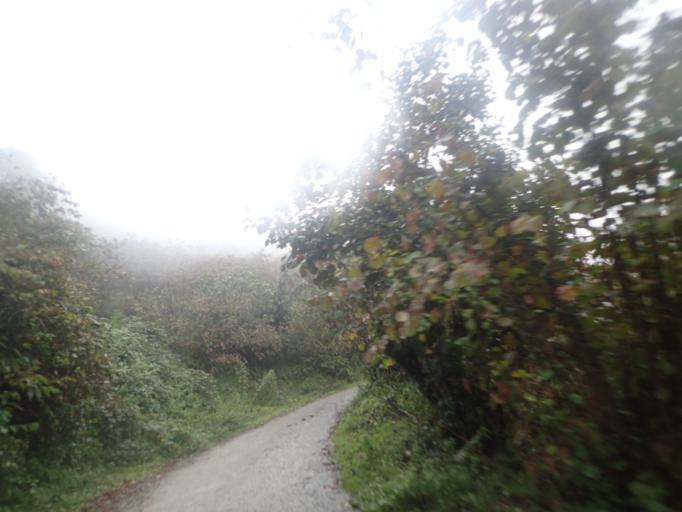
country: TR
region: Ordu
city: Persembe
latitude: 41.0377
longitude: 37.7195
